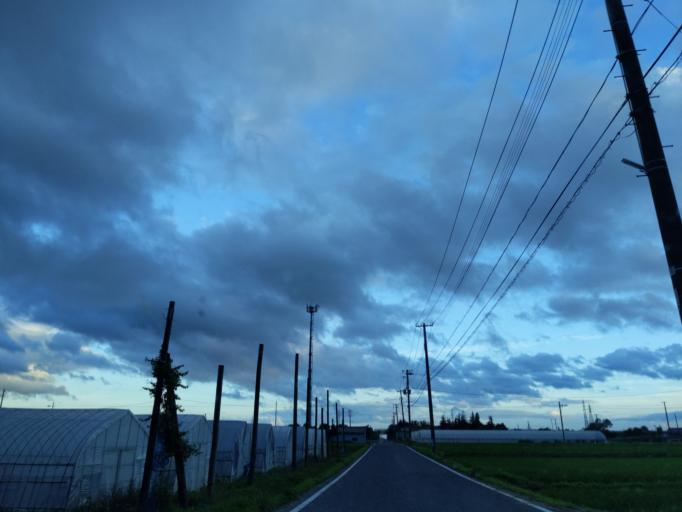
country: JP
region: Fukushima
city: Motomiya
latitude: 37.4657
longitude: 140.3697
